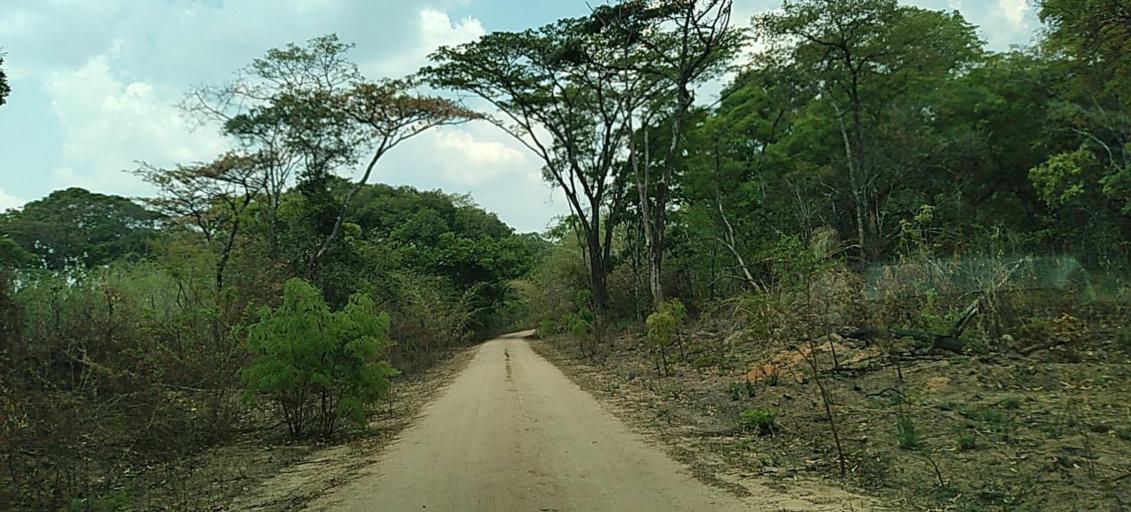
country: ZM
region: Copperbelt
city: Chingola
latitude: -12.7543
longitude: 27.7151
